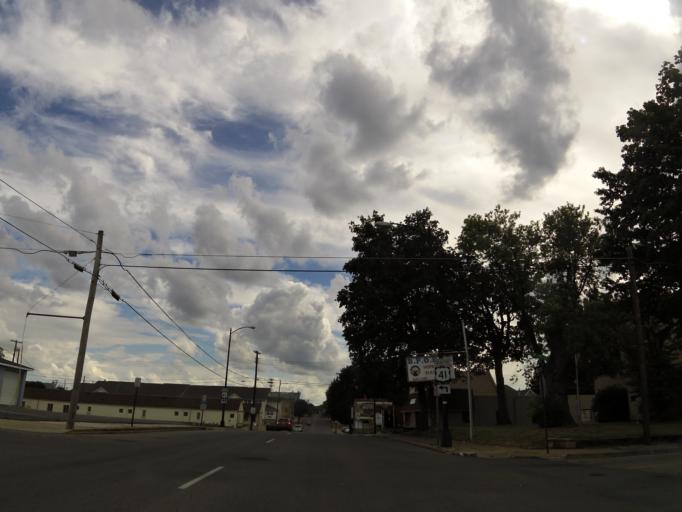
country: US
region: Kentucky
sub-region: Christian County
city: Hopkinsville
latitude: 36.8692
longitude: -87.4864
